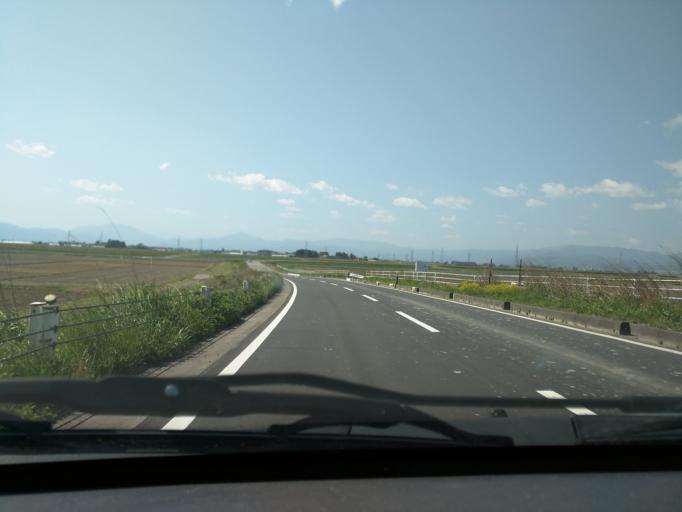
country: JP
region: Fukushima
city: Kitakata
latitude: 37.5862
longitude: 139.8699
